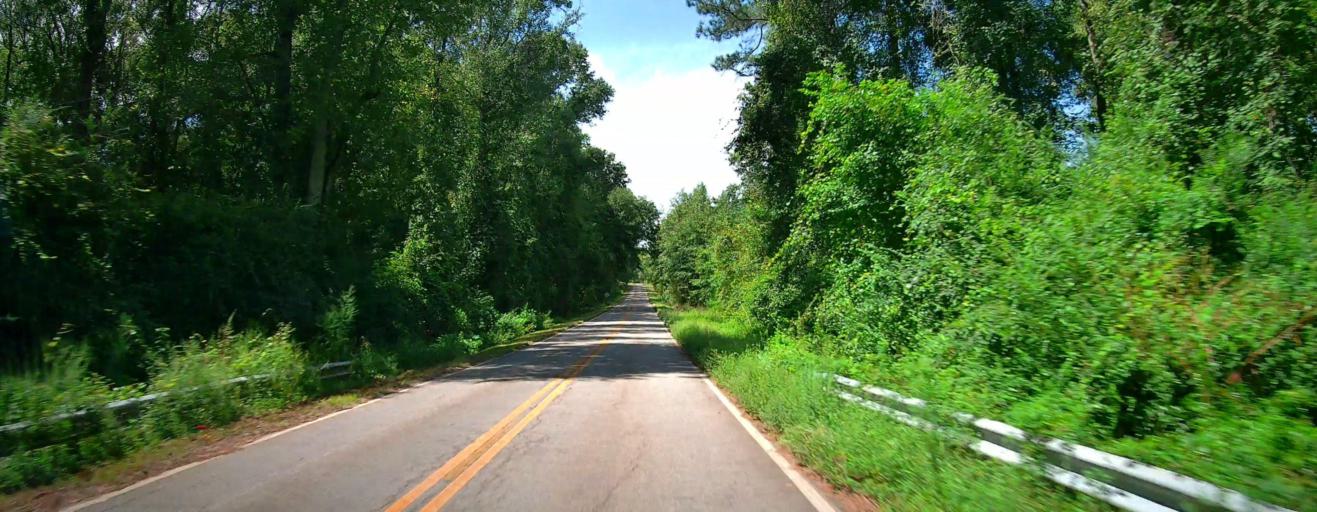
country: US
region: Georgia
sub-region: Peach County
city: Fort Valley
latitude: 32.5338
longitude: -83.8106
